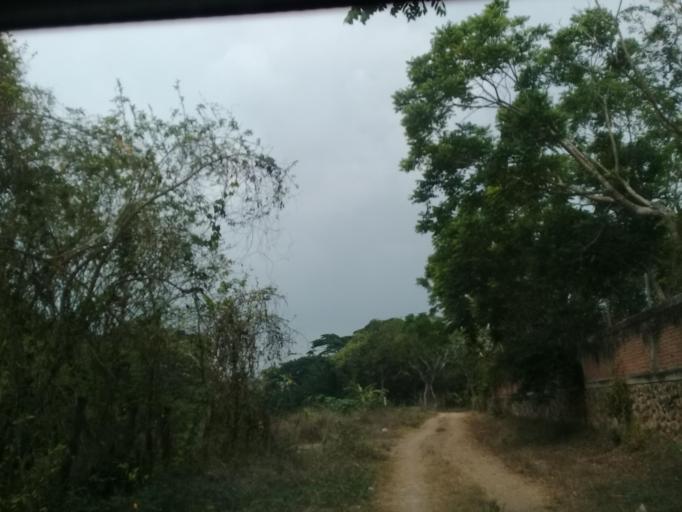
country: MX
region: Veracruz
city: El Tejar
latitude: 19.0510
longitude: -96.1968
